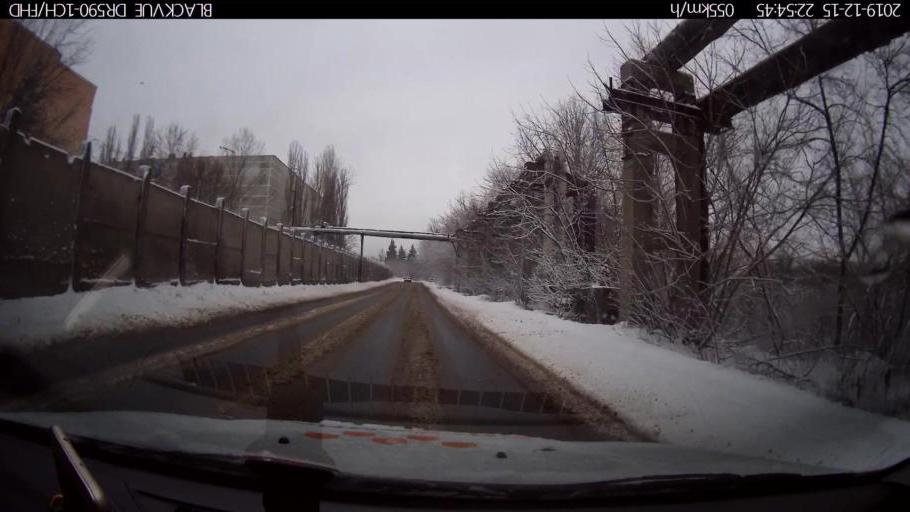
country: RU
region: Nizjnij Novgorod
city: Neklyudovo
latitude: 56.3577
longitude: 43.8844
